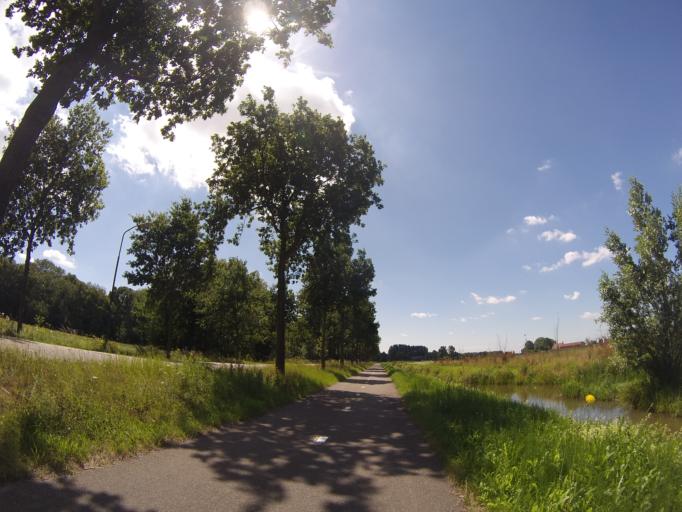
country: NL
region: Utrecht
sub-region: Stichtse Vecht
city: Spechtenkamp
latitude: 52.1271
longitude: 4.9841
